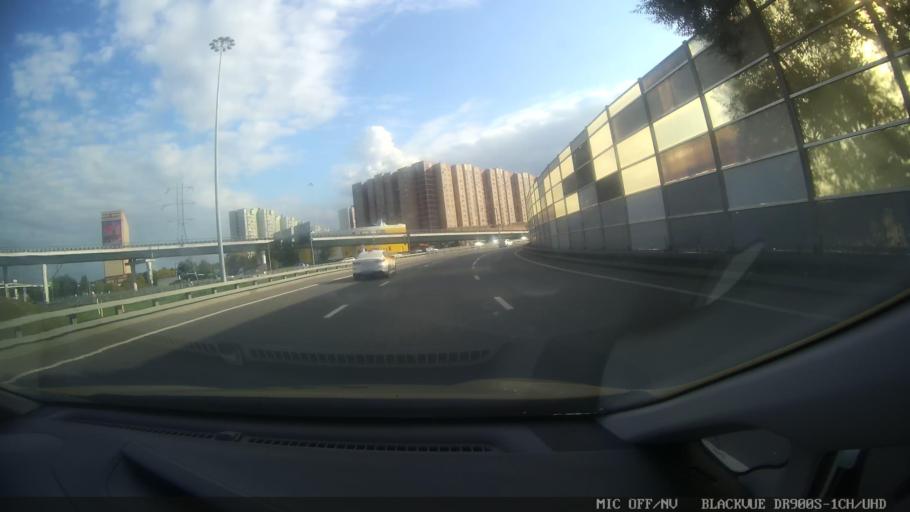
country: RU
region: Moscow
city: Yaroslavskiy
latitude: 55.8816
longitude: 37.7209
